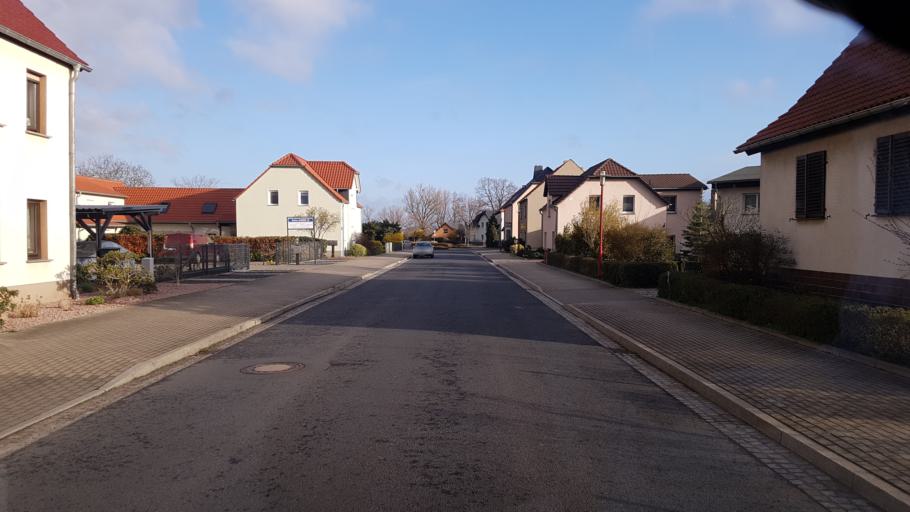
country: DE
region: Saxony
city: Nauwalde
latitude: 51.4181
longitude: 13.4442
